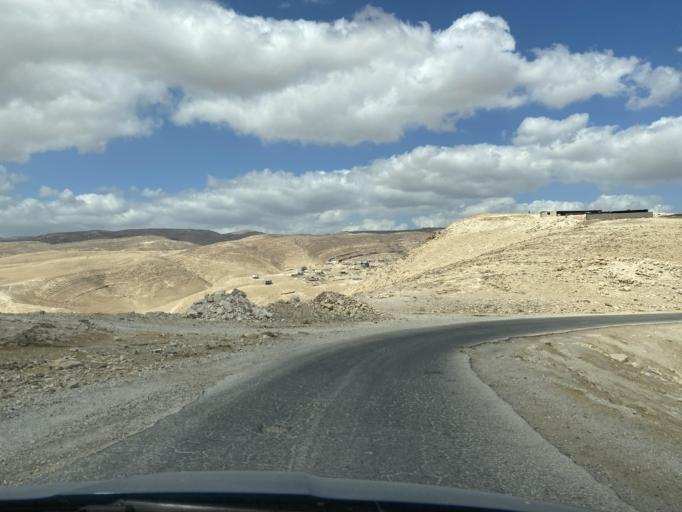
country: PS
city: `Arab ar Rashaydah
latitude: 31.5585
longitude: 35.2460
